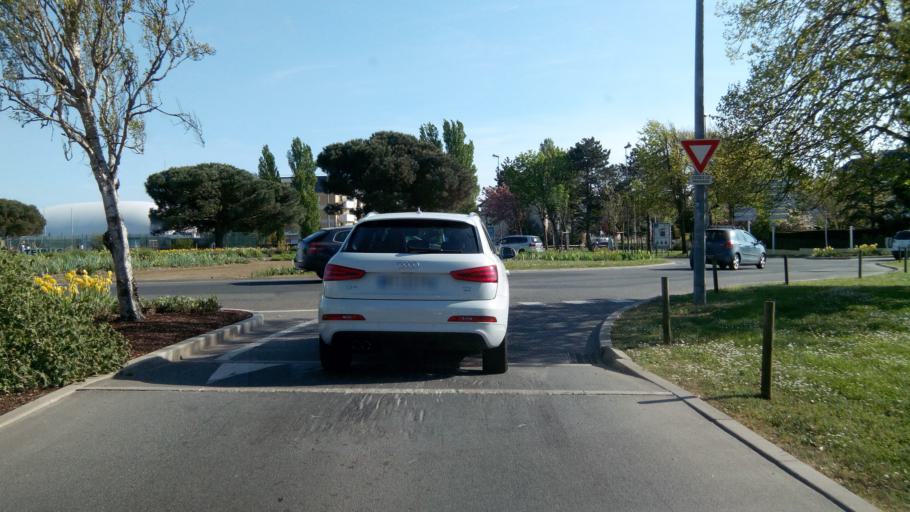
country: FR
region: Pays de la Loire
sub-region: Departement de la Loire-Atlantique
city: Pornichet
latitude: 47.2613
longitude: -2.3345
